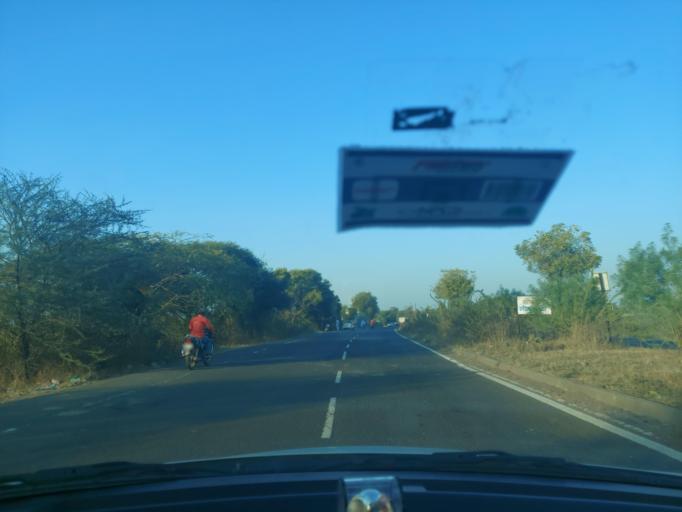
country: IN
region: Madhya Pradesh
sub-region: Indore
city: Sanwer
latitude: 23.0386
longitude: 75.8279
